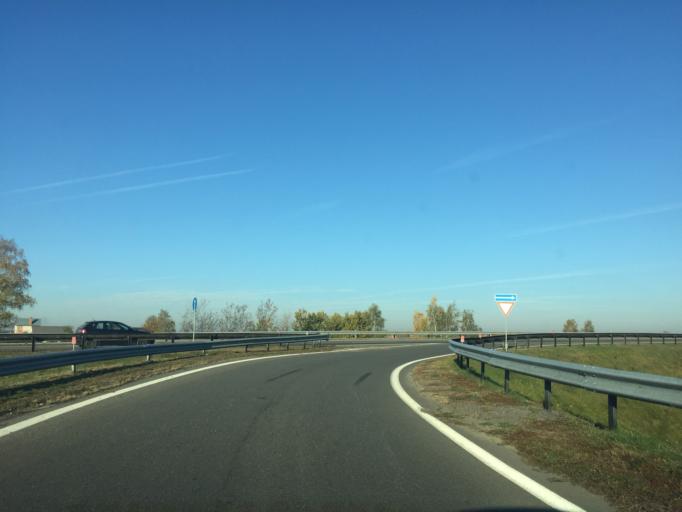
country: BY
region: Minsk
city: Luhavaya Slabada
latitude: 53.7896
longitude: 27.8209
